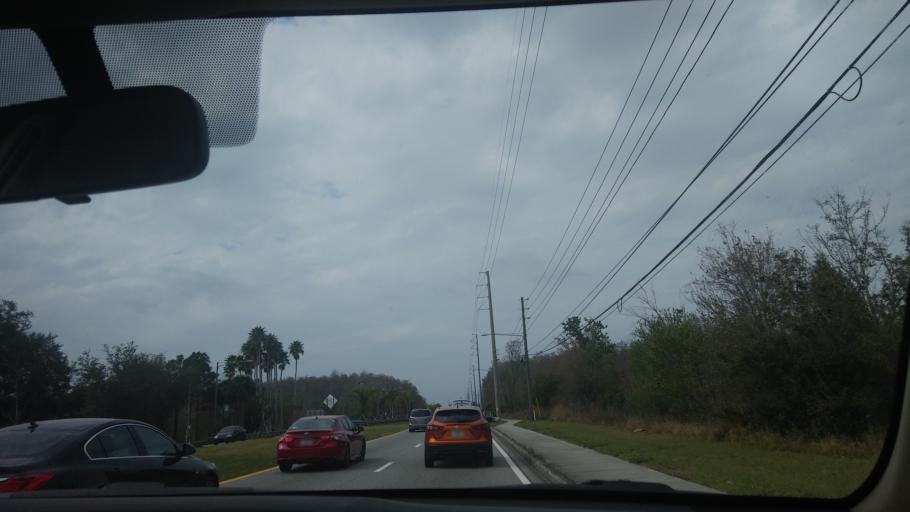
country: US
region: Florida
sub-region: Orange County
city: Williamsburg
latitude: 28.4105
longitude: -81.4317
